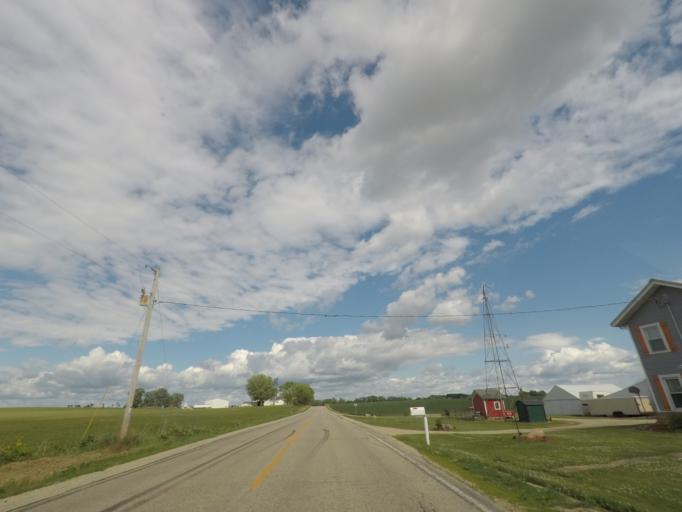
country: US
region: Wisconsin
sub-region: Rock County
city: Orfordville
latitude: 42.7066
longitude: -89.1704
